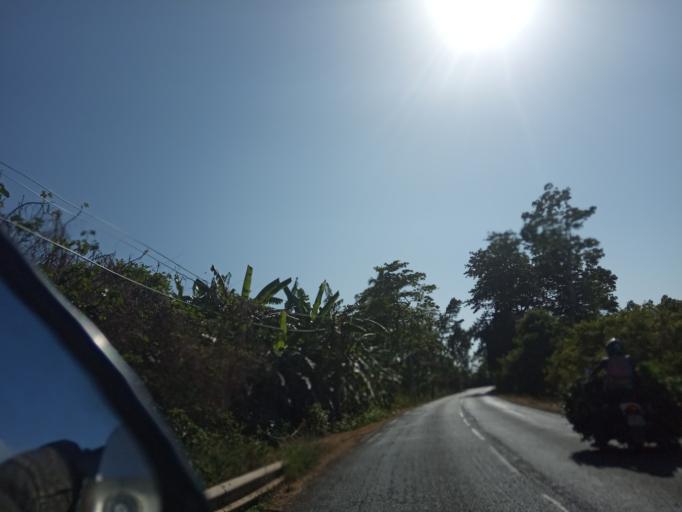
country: YT
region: Bandrele
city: Bandrele
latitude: -12.8970
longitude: 45.1956
